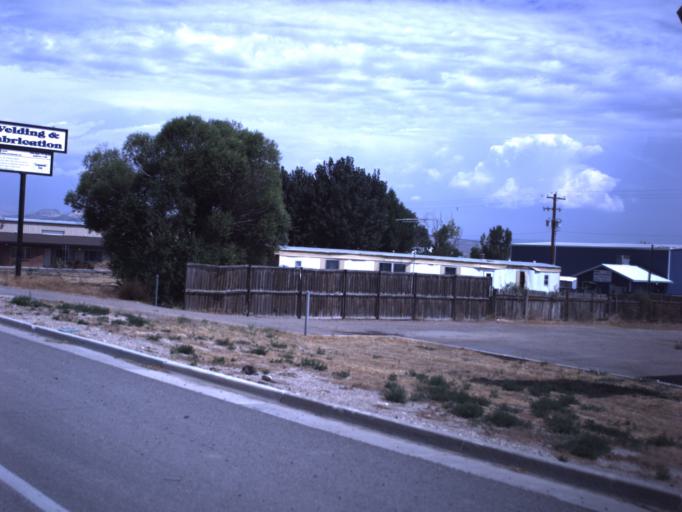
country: US
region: Utah
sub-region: Uintah County
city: Naples
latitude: 40.4441
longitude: -109.4997
